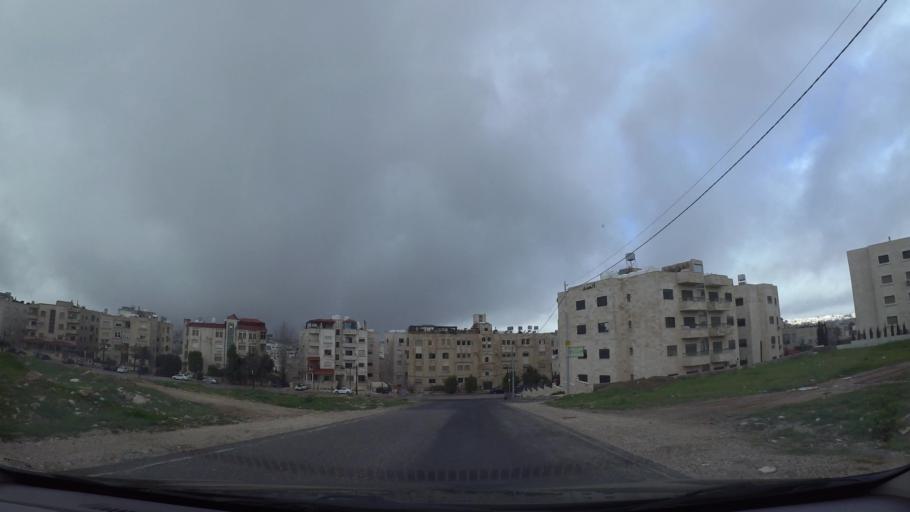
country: JO
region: Amman
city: Wadi as Sir
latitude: 31.9421
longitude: 35.8555
